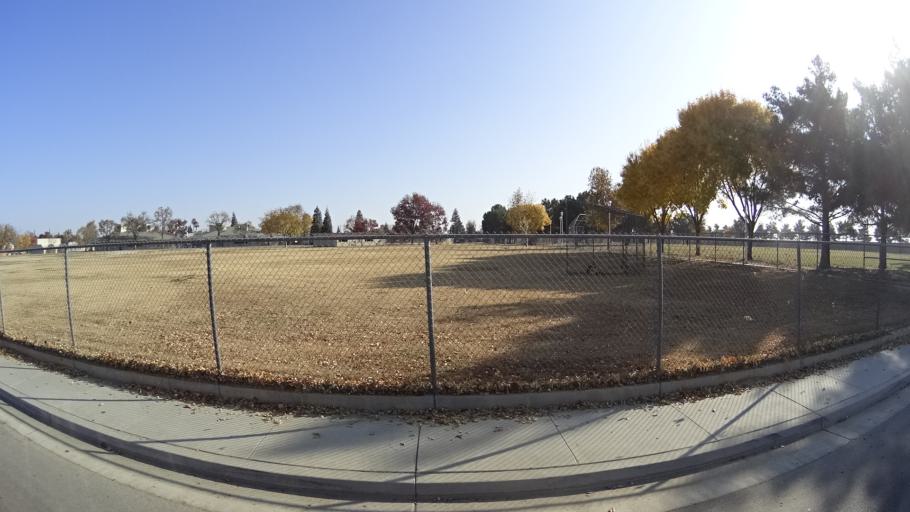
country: US
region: California
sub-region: Kern County
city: Greenacres
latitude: 35.3638
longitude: -119.1063
